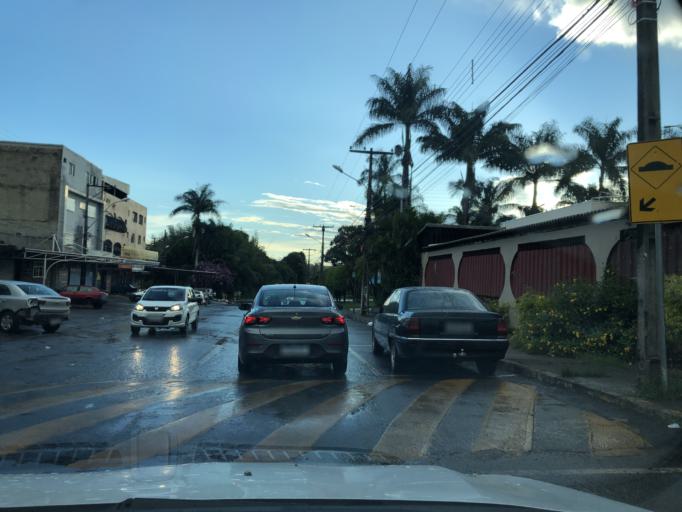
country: BR
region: Federal District
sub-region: Brasilia
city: Brasilia
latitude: -15.8719
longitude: -47.9645
